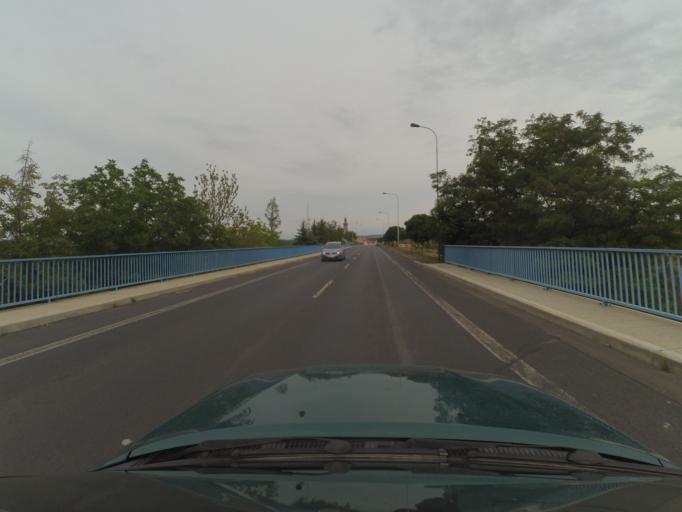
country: CZ
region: Ustecky
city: Cerncice
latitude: 50.3608
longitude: 13.8377
